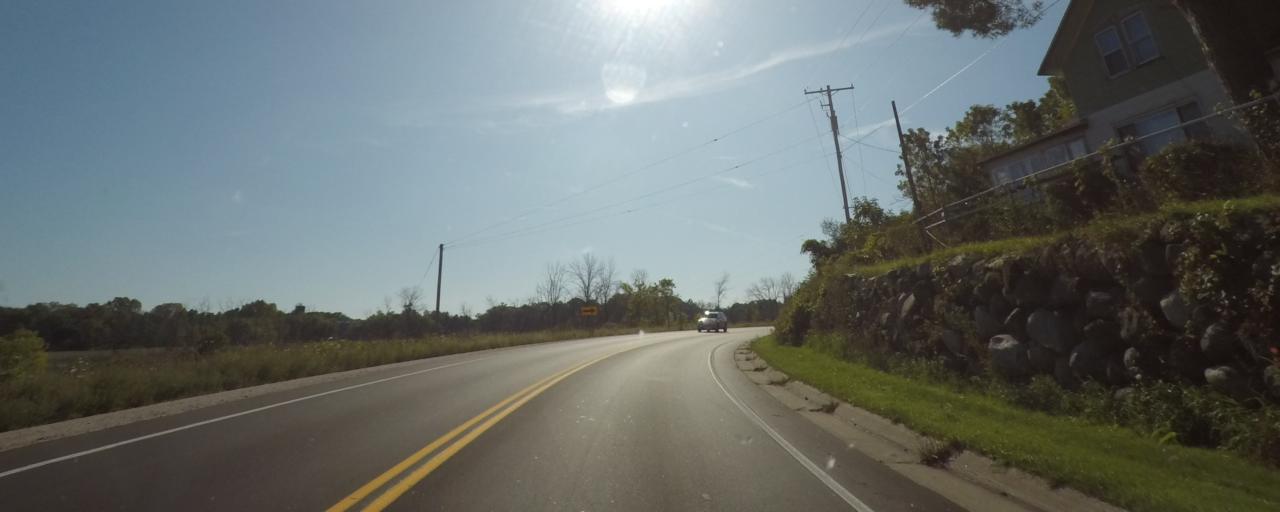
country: US
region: Wisconsin
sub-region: Jefferson County
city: Johnson Creek
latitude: 43.0161
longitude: -88.7063
